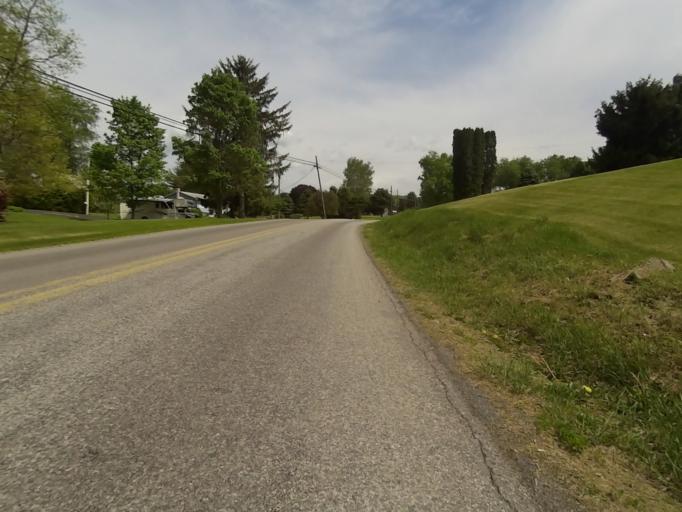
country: US
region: Pennsylvania
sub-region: Centre County
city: Zion
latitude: 40.9836
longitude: -77.6316
